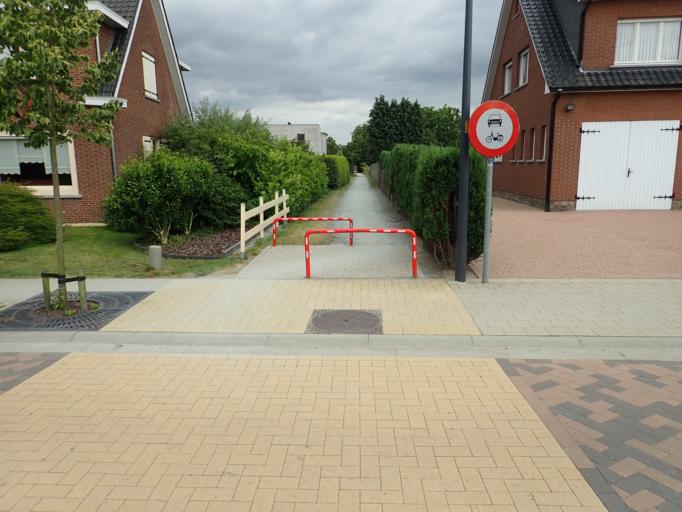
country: BE
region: Flanders
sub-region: Provincie Antwerpen
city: Oostmalle
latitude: 51.3041
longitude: 4.7404
